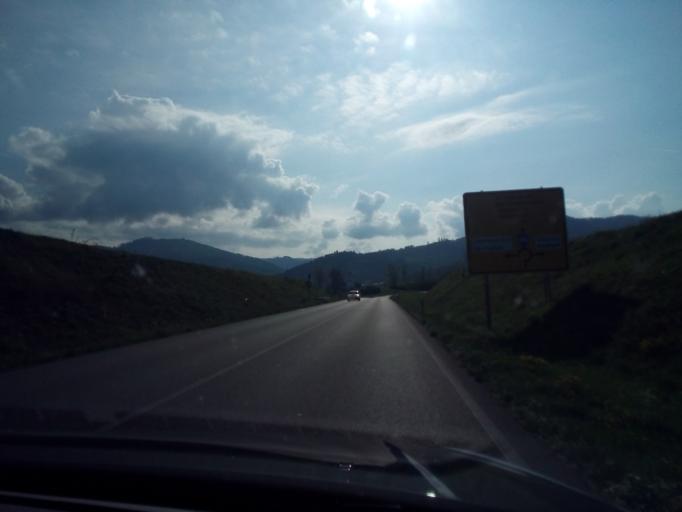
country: DE
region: Baden-Wuerttemberg
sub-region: Freiburg Region
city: Oberkirch
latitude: 48.5205
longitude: 8.0863
